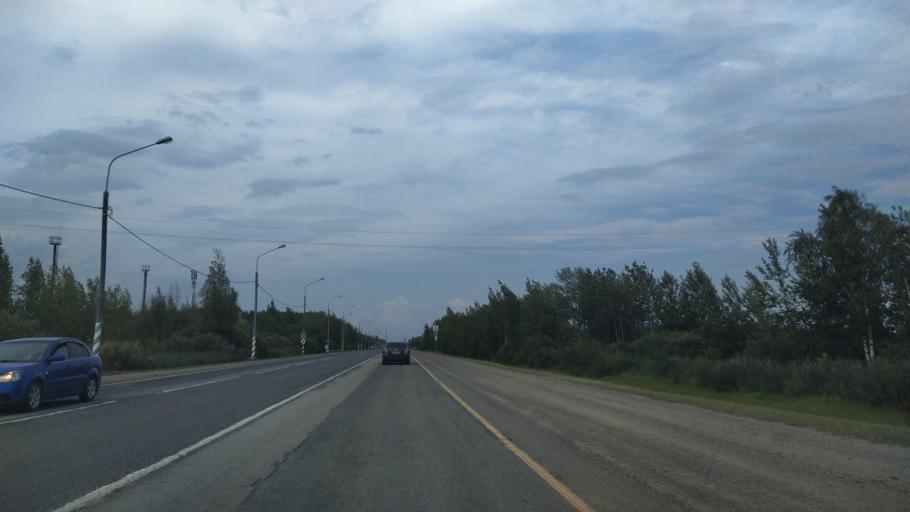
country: RU
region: Novgorod
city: Pankovka
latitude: 58.4673
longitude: 31.1622
